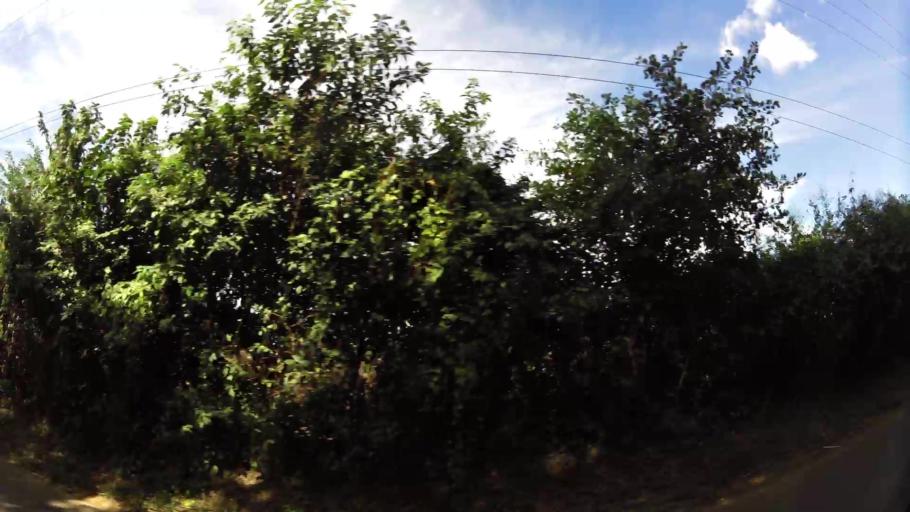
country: SV
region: San Salvador
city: Aguilares
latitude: 13.9567
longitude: -89.1448
